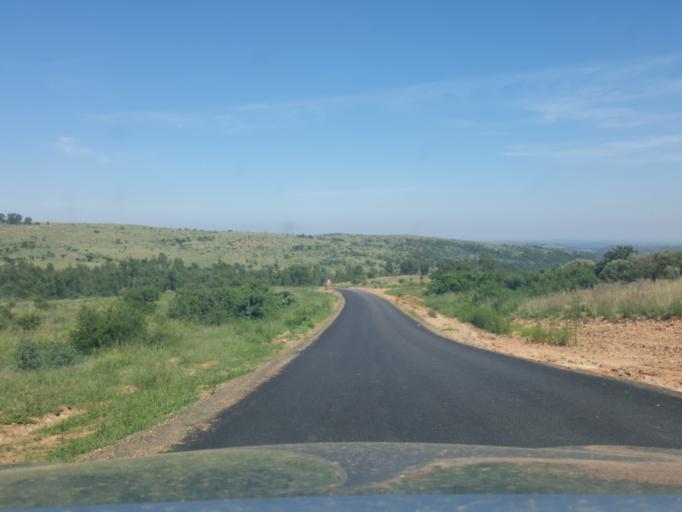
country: ZA
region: Gauteng
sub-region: City of Tshwane Metropolitan Municipality
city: Cullinan
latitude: -25.6866
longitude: 28.5231
